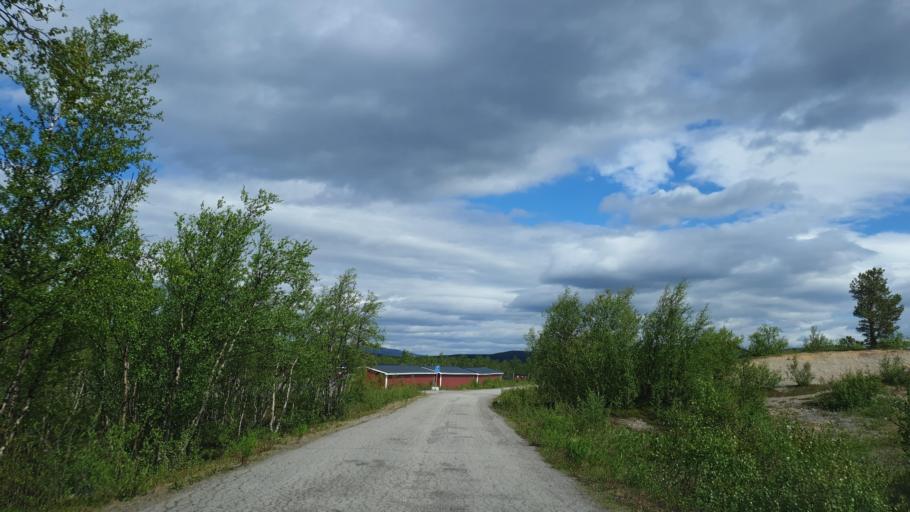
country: SE
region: Norrbotten
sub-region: Kiruna Kommun
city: Kiruna
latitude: 68.2252
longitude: 19.7177
